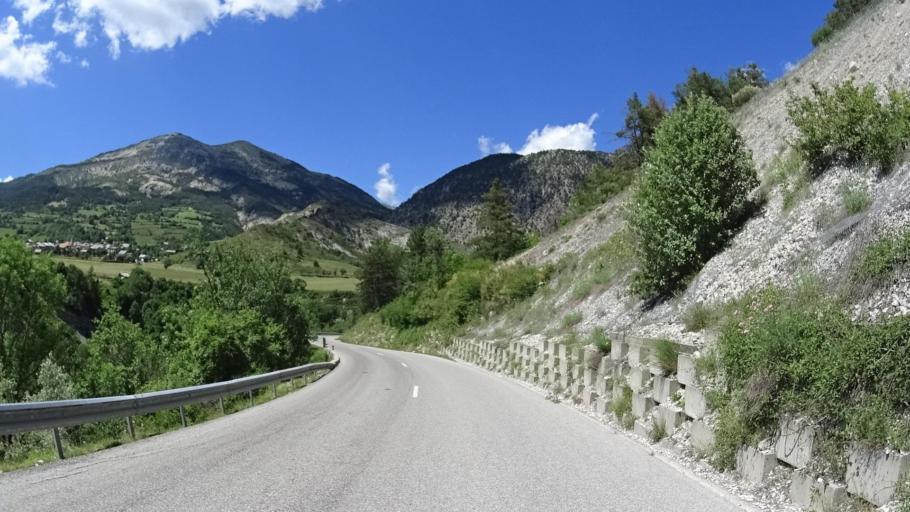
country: FR
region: Provence-Alpes-Cote d'Azur
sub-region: Departement des Alpes-de-Haute-Provence
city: Annot
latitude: 44.0930
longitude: 6.5655
